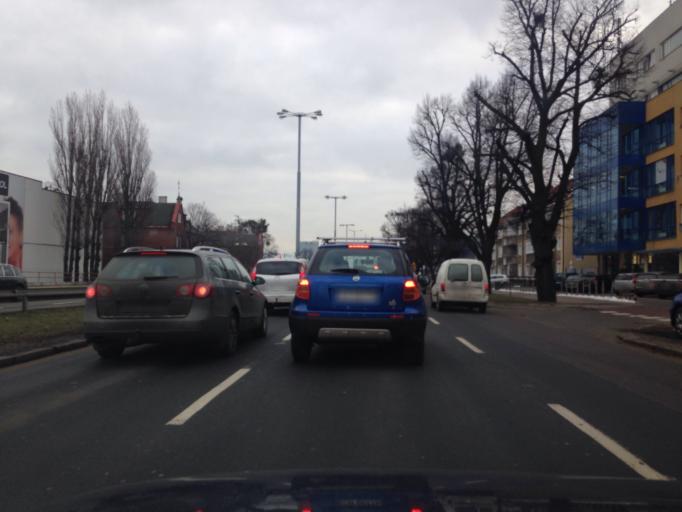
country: PL
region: Pomeranian Voivodeship
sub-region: Sopot
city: Sopot
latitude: 54.3884
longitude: 18.5892
